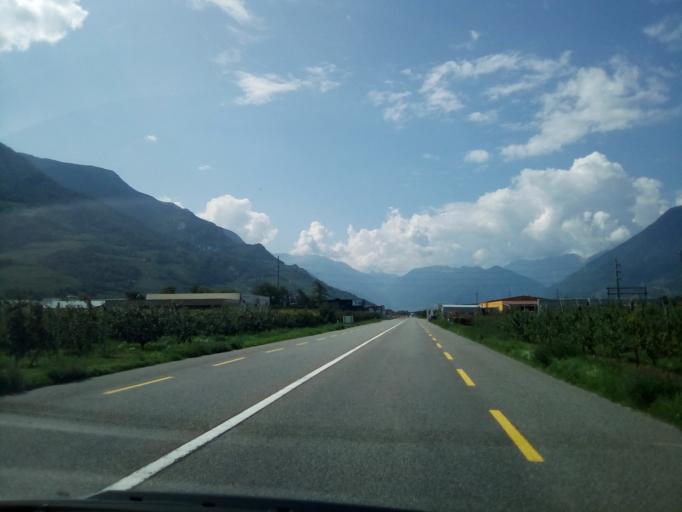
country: CH
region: Valais
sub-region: Martigny District
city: Saillon
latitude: 46.1625
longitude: 7.2019
